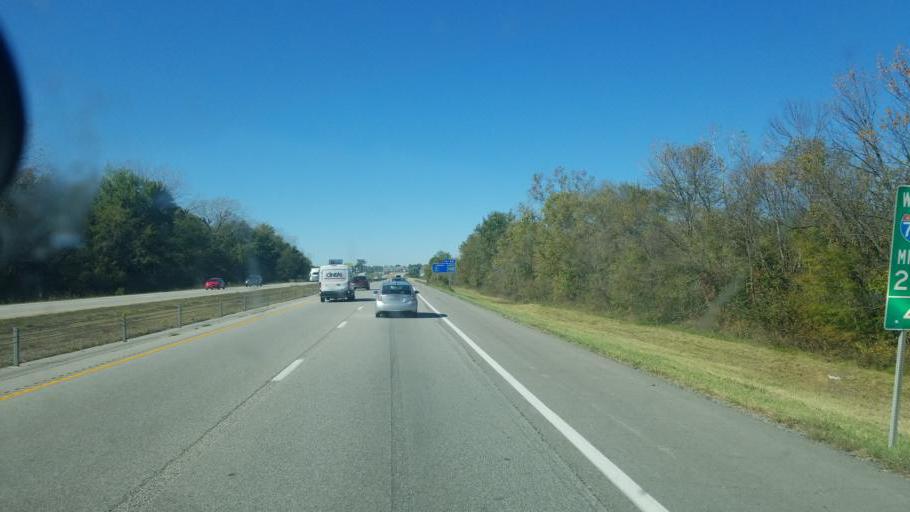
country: US
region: Missouri
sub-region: Jackson County
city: Grain Valley
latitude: 39.0205
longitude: -94.1795
